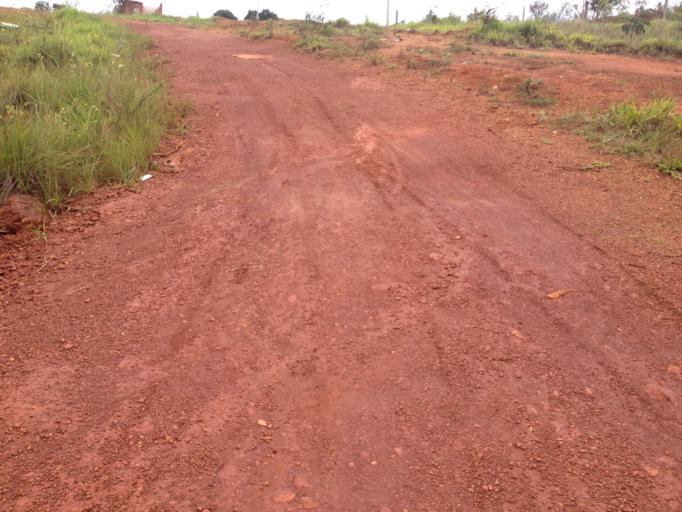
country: BR
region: Federal District
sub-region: Brasilia
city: Brasilia
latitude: -15.5873
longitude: -48.2675
